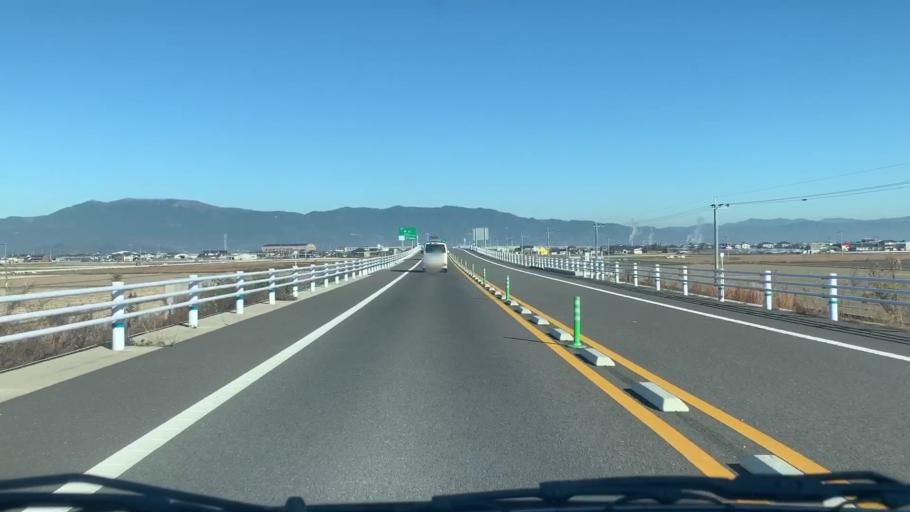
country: JP
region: Saga Prefecture
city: Saga-shi
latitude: 33.2125
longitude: 130.2146
